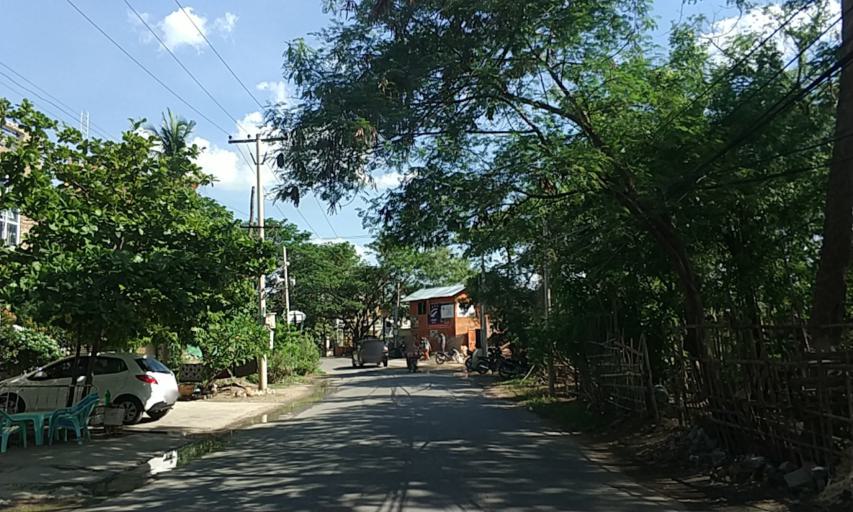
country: MM
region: Mandalay
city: Mandalay
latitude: 21.9714
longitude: 96.1076
